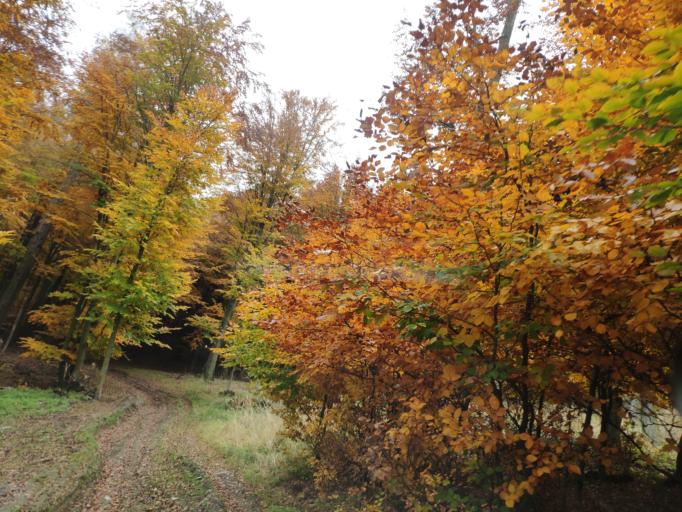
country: SK
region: Kosicky
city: Moldava nad Bodvou
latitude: 48.7314
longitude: 21.0194
